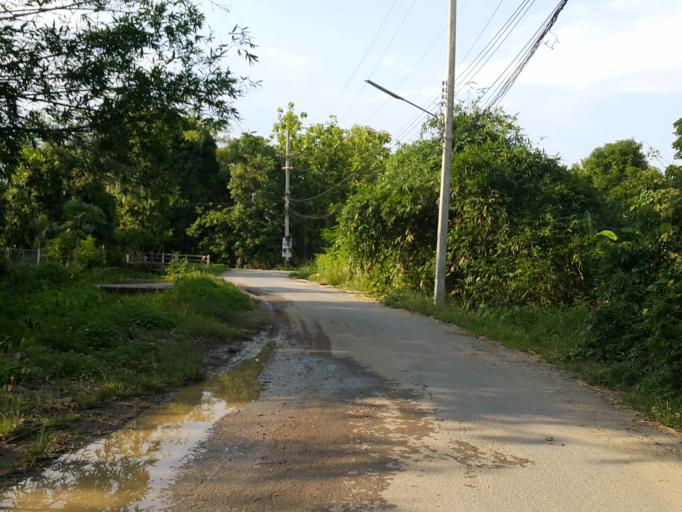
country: TH
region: Chiang Mai
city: San Sai
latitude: 18.8437
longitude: 99.0963
